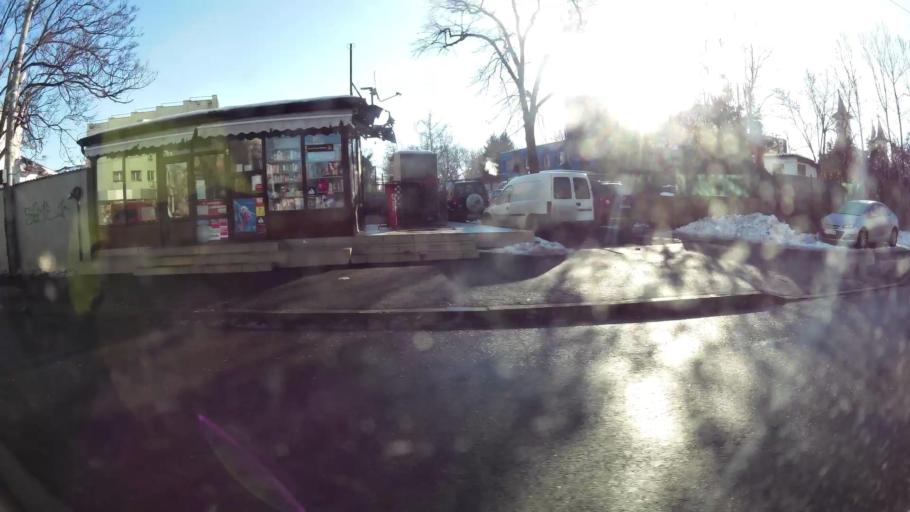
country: RO
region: Bucuresti
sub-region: Municipiul Bucuresti
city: Bucuresti
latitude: 44.4079
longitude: 26.0963
